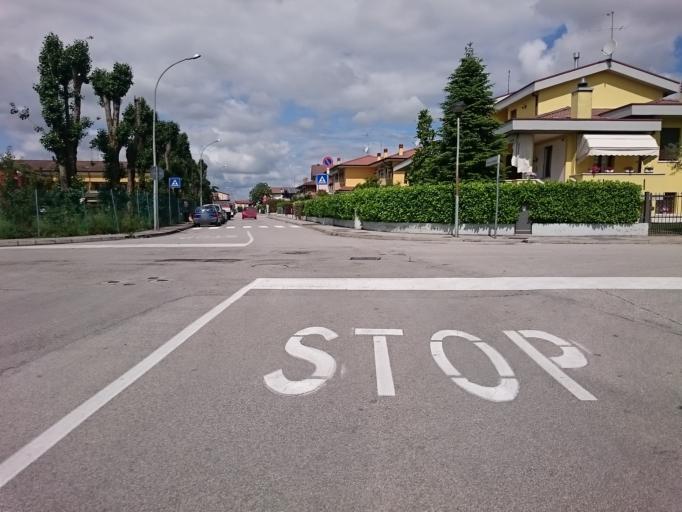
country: IT
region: Veneto
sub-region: Provincia di Padova
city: Mestrino
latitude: 45.4444
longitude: 11.7622
